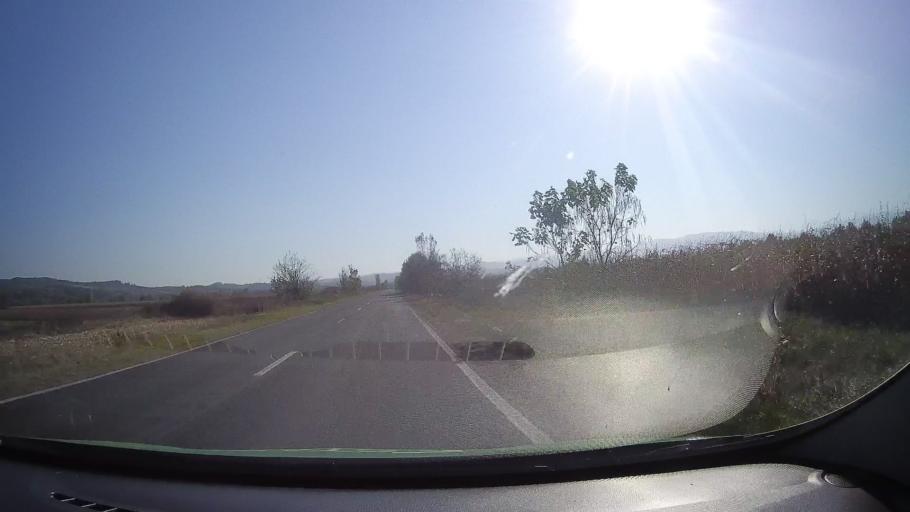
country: RO
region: Timis
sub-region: Comuna Margina
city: Margina
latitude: 45.8552
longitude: 22.2788
